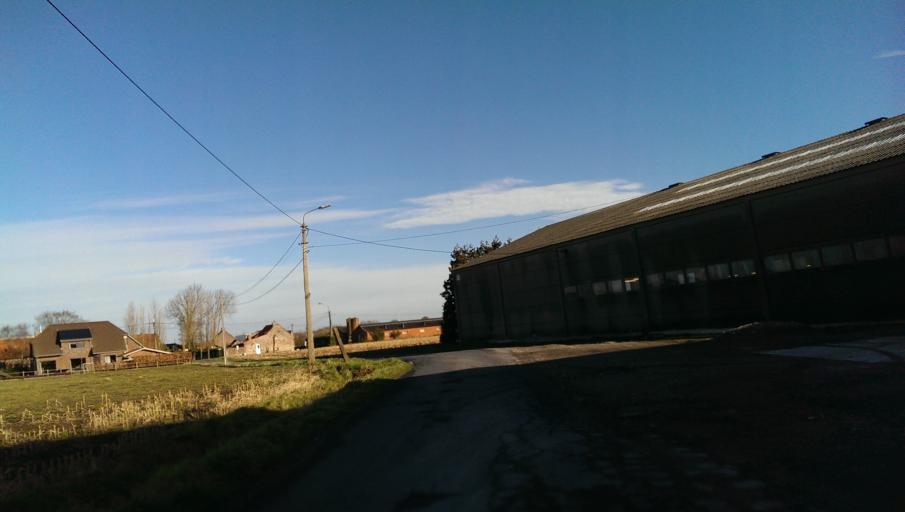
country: BE
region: Flanders
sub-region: Provincie West-Vlaanderen
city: Hooglede
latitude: 50.9489
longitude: 3.0828
